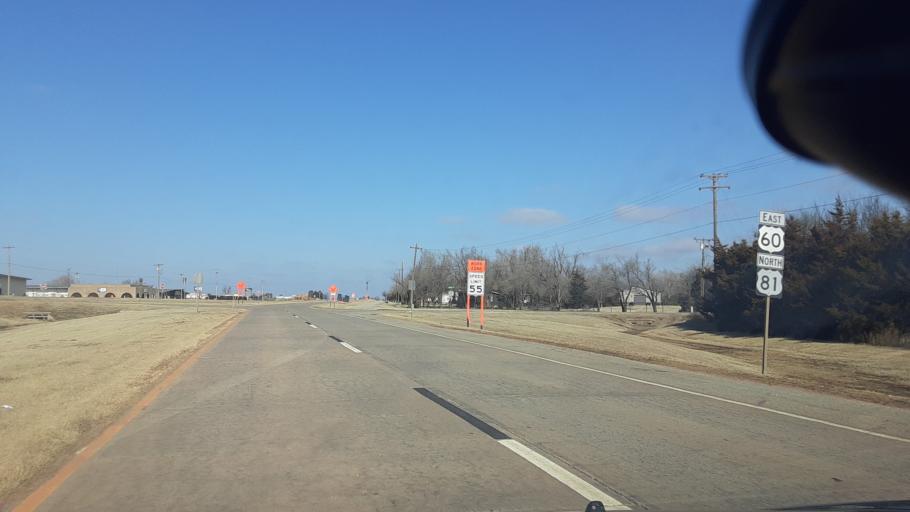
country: US
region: Oklahoma
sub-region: Garfield County
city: Enid
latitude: 36.4481
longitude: -97.8727
